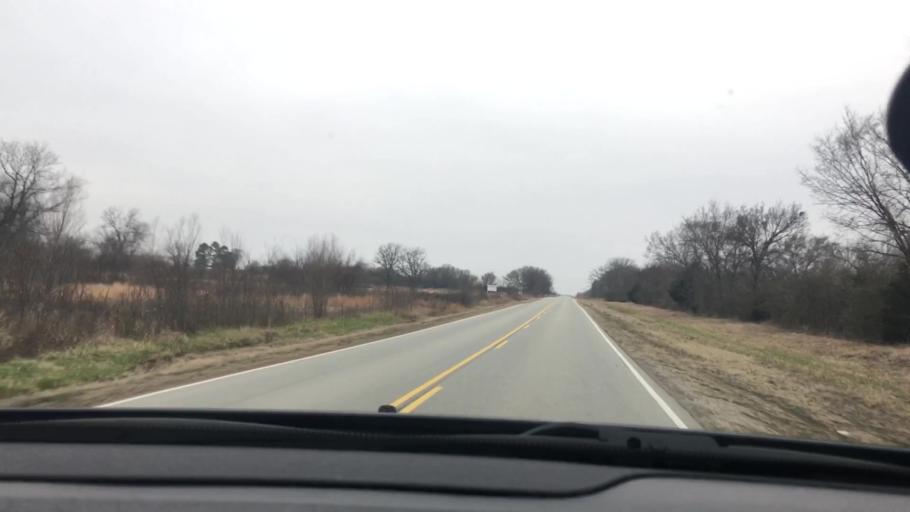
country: US
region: Oklahoma
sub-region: Coal County
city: Coalgate
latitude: 34.5297
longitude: -96.2635
